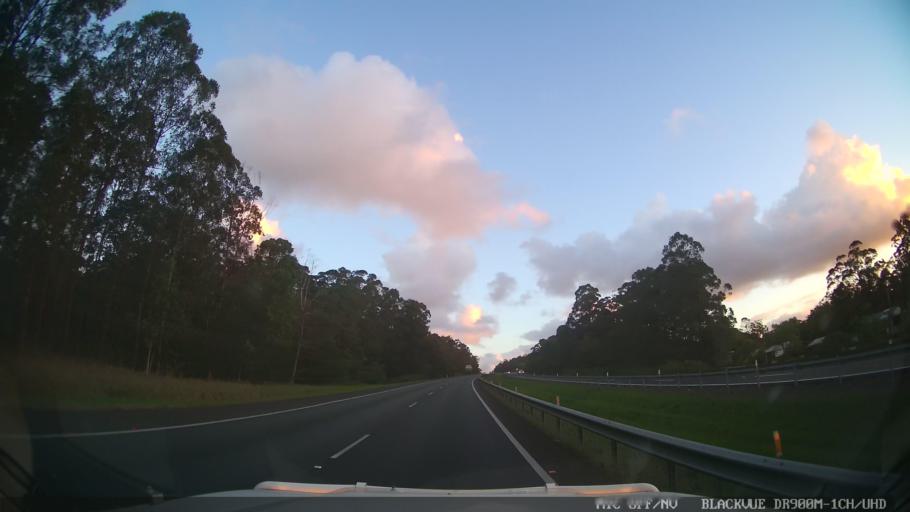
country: AU
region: Queensland
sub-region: Sunshine Coast
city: Yandina
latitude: -26.5869
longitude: 152.9680
